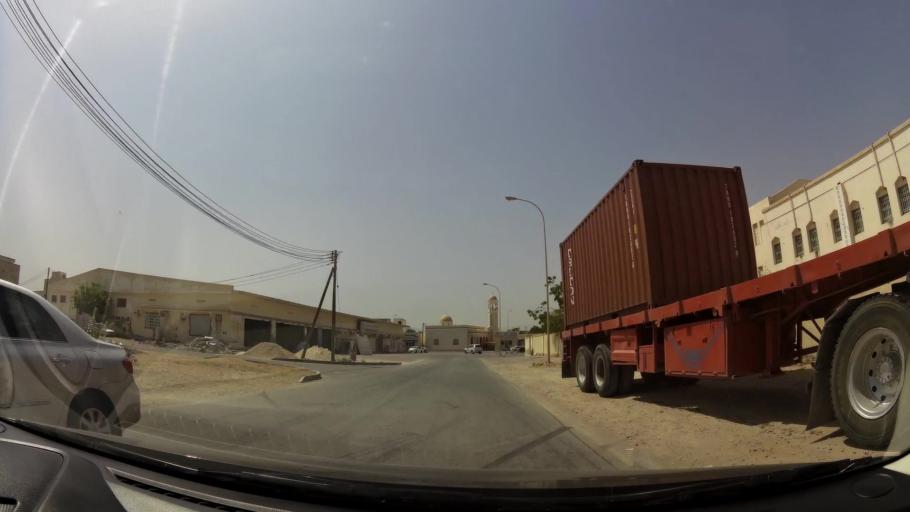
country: OM
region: Zufar
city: Salalah
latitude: 17.0109
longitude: 54.0745
